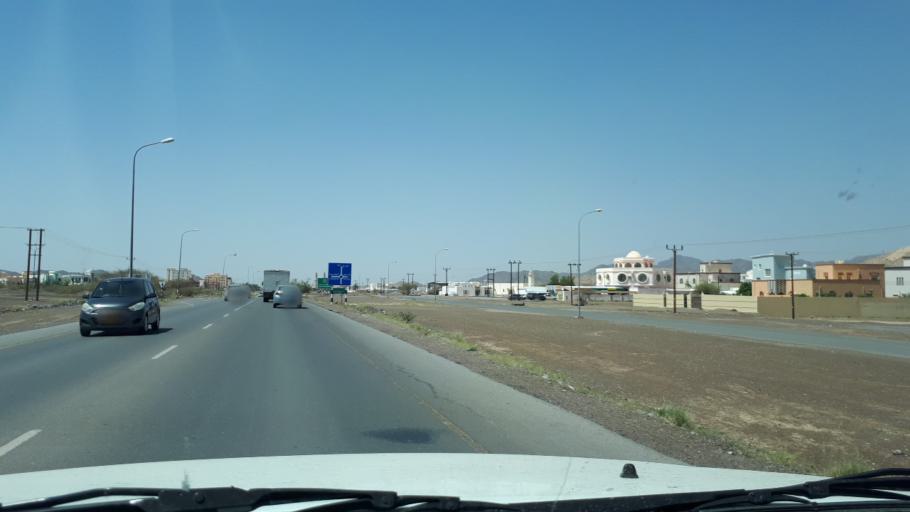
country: OM
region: Muhafazat ad Dakhiliyah
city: Bahla'
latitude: 23.0075
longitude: 57.3224
